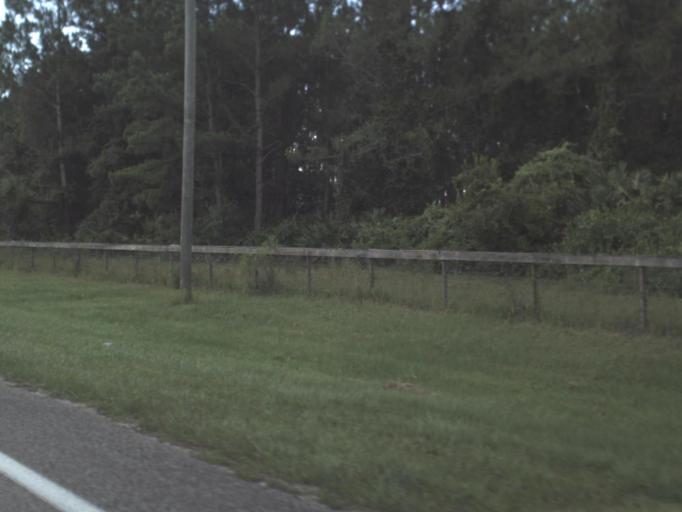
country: US
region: Florida
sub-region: Putnam County
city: East Palatka
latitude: 29.5634
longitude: -81.5433
